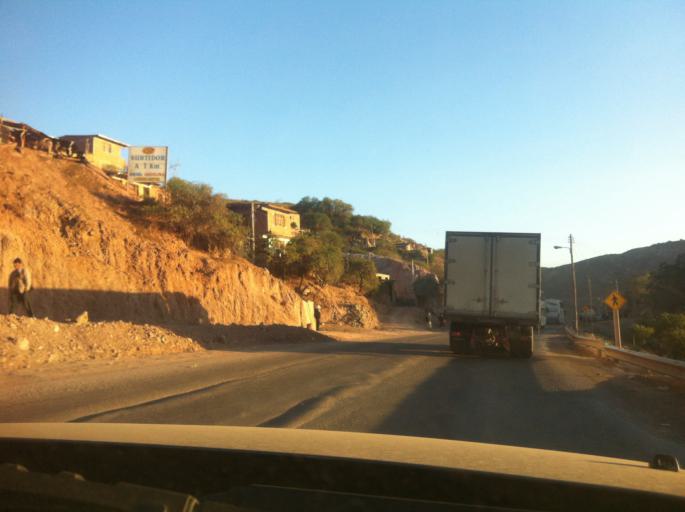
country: BO
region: Cochabamba
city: Sipe Sipe
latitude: -17.5672
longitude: -66.3473
